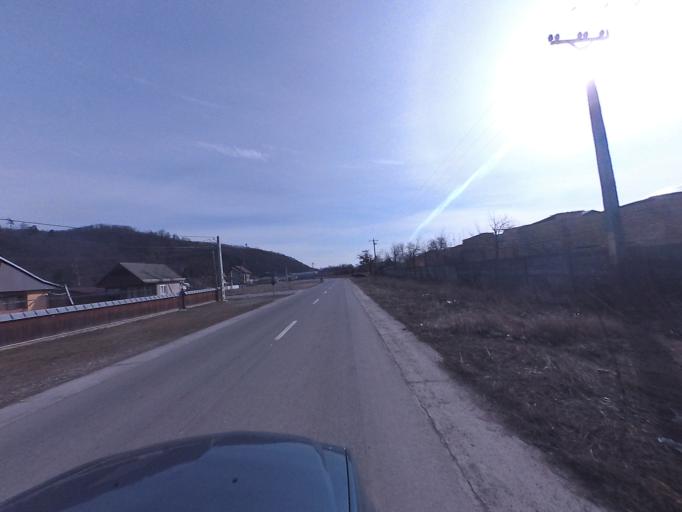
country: RO
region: Neamt
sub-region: Oras Targu Neamt
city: Humulesti
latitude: 47.2111
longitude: 26.3400
